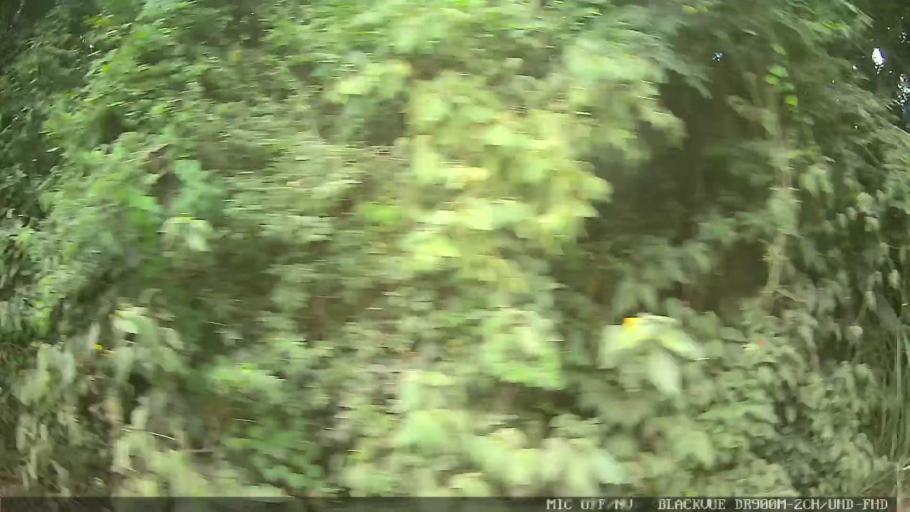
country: BR
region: Sao Paulo
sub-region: Bom Jesus Dos Perdoes
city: Bom Jesus dos Perdoes
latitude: -23.1236
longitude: -46.4971
